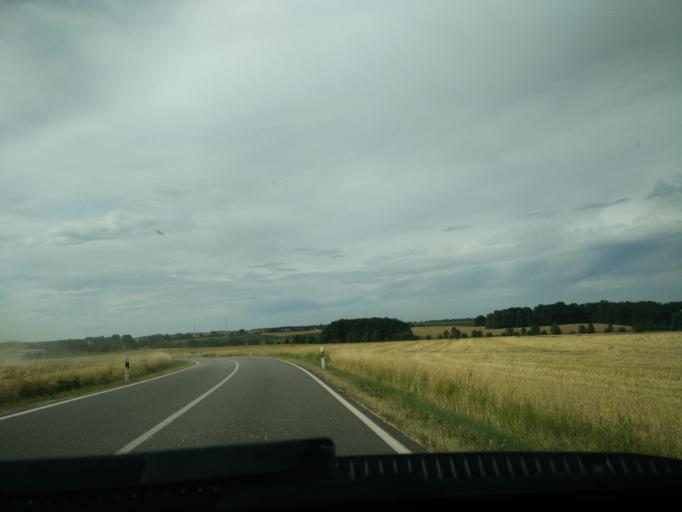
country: DE
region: Saxony
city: Bad Lausick
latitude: 51.1029
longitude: 12.6187
